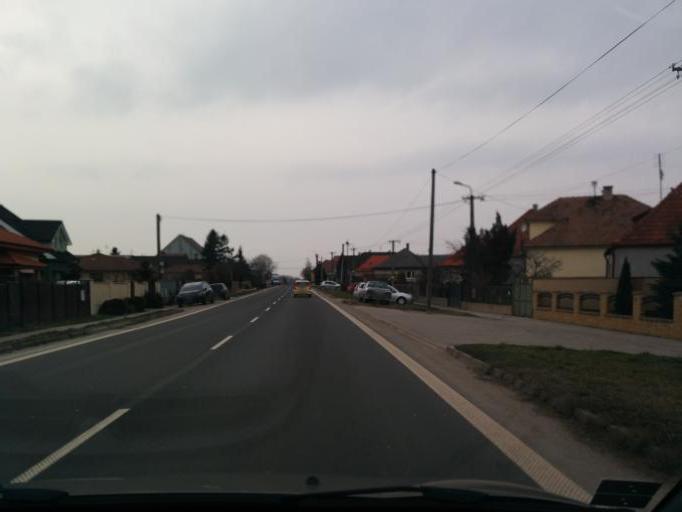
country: SK
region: Trnavsky
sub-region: Okres Galanta
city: Galanta
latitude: 48.2840
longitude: 17.7657
